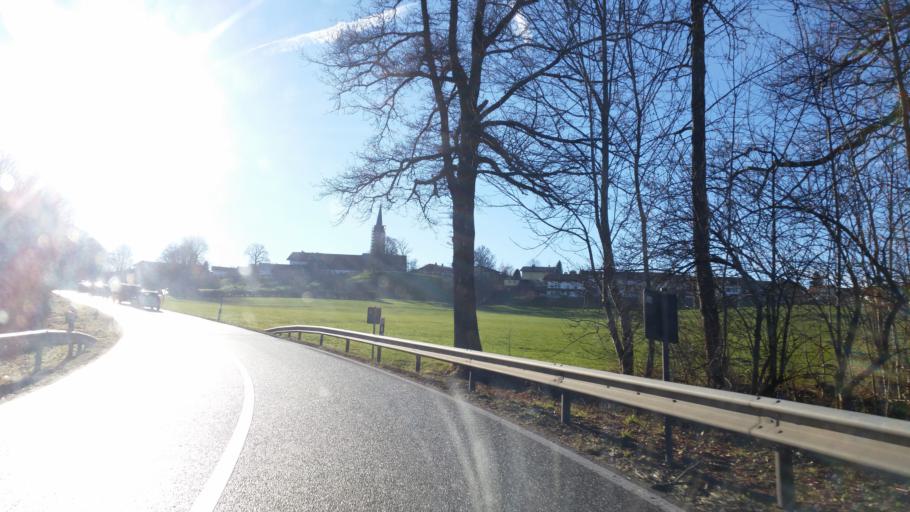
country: DE
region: Bavaria
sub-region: Upper Bavaria
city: Irschenberg
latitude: 47.8385
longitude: 11.9178
